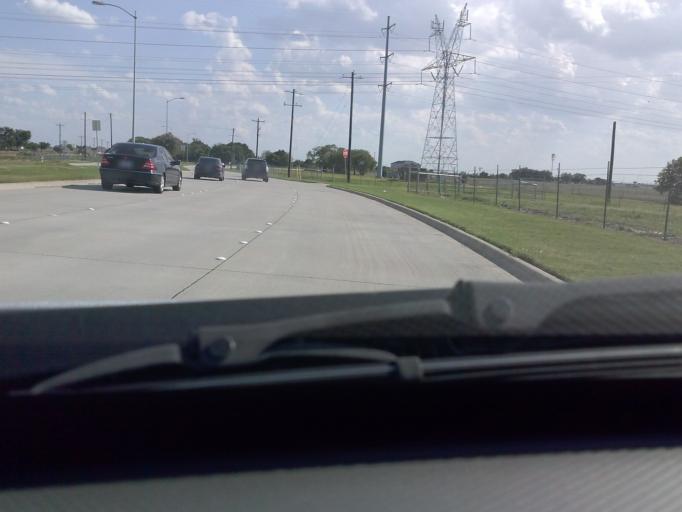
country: US
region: Texas
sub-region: Denton County
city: The Colony
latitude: 33.0615
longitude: -96.8234
